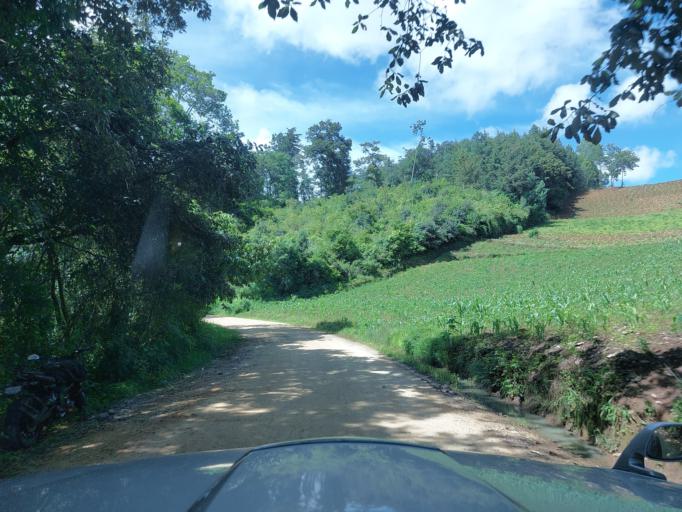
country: GT
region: Chimaltenango
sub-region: Municipio de San Juan Comalapa
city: Comalapa
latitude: 14.7542
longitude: -90.8716
